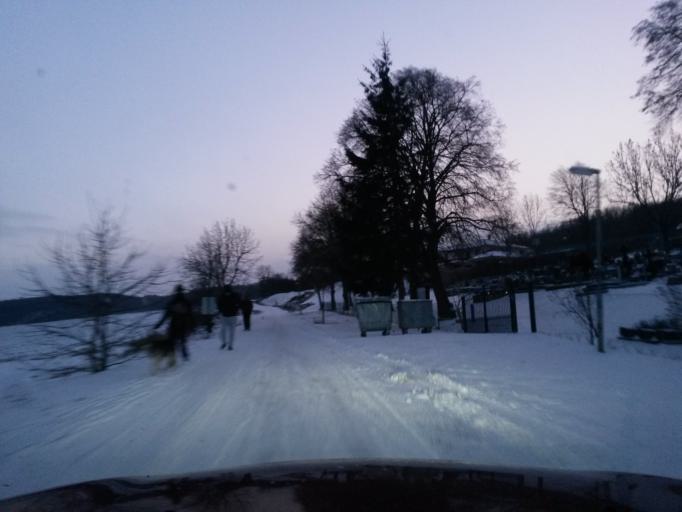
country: SK
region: Kosicky
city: Kosice
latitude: 48.7445
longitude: 21.3190
